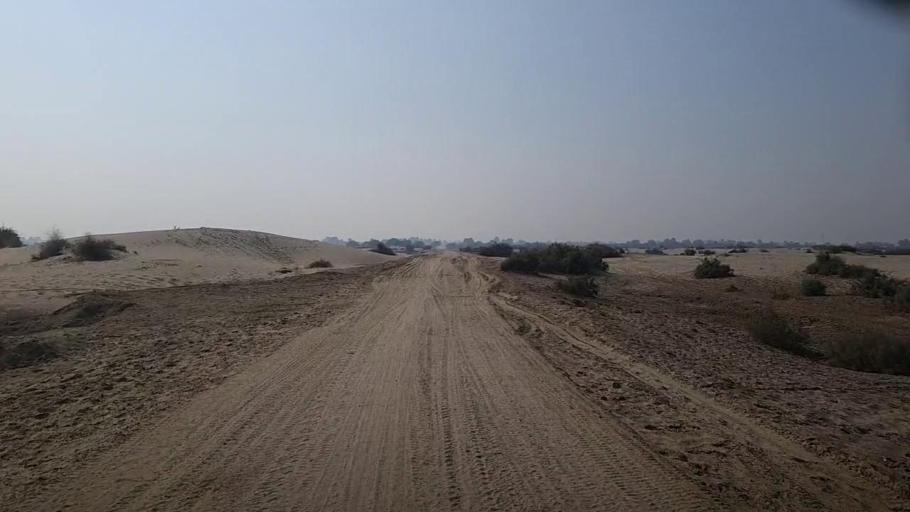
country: PK
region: Sindh
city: Bozdar
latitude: 27.2206
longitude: 68.5836
